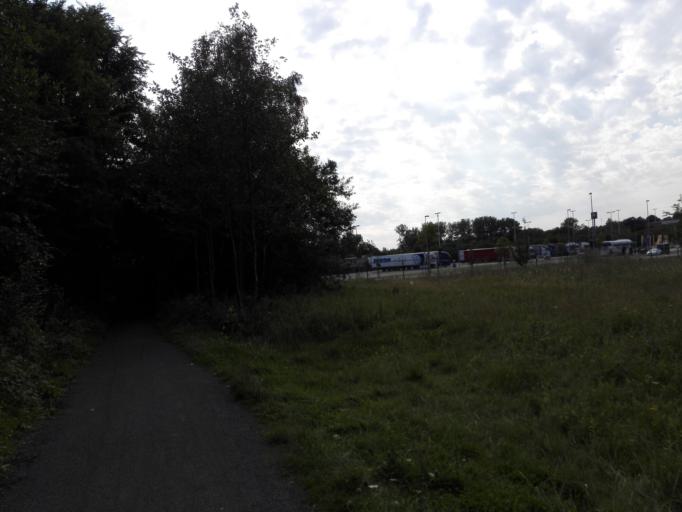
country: BE
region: Flanders
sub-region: Provincie Vlaams-Brabant
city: Oud-Heverlee
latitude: 50.8538
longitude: 4.6618
